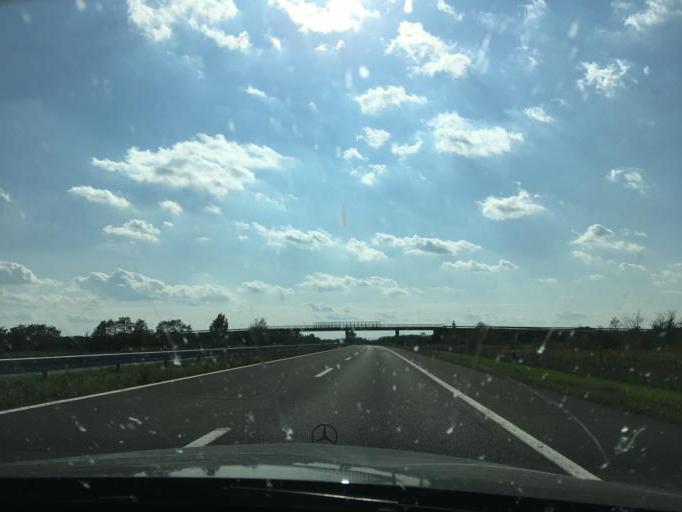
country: HR
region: Medimurska
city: Palovec
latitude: 46.3990
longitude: 16.5713
